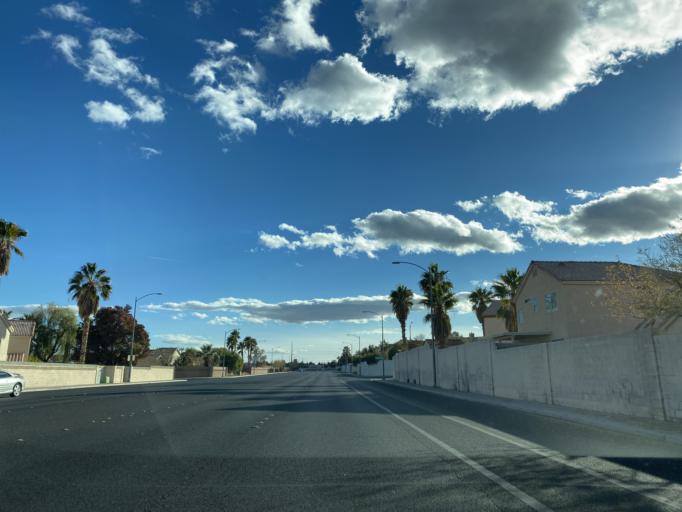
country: US
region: Nevada
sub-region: Clark County
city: Summerlin South
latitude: 36.2233
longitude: -115.2974
